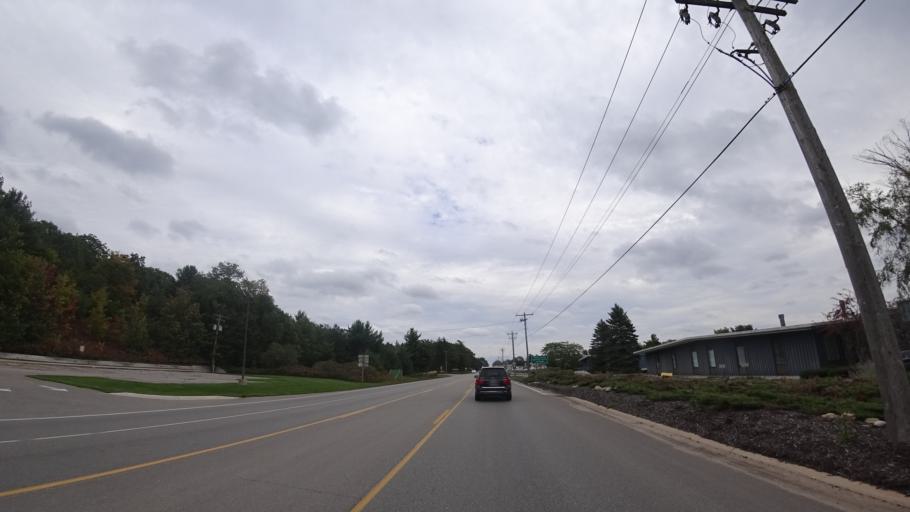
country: US
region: Michigan
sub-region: Emmet County
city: Petoskey
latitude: 45.4279
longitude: -84.9119
